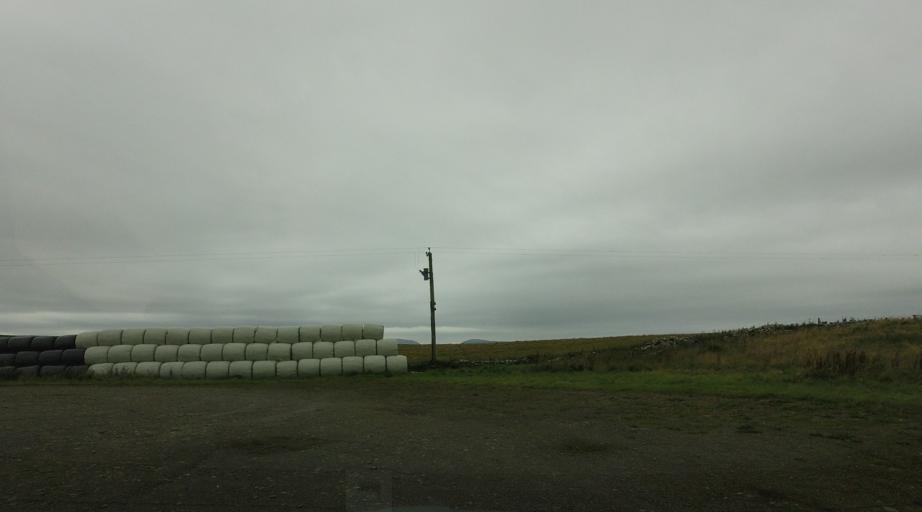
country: GB
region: Scotland
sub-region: Orkney Islands
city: Stromness
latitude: 58.9932
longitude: -3.2018
